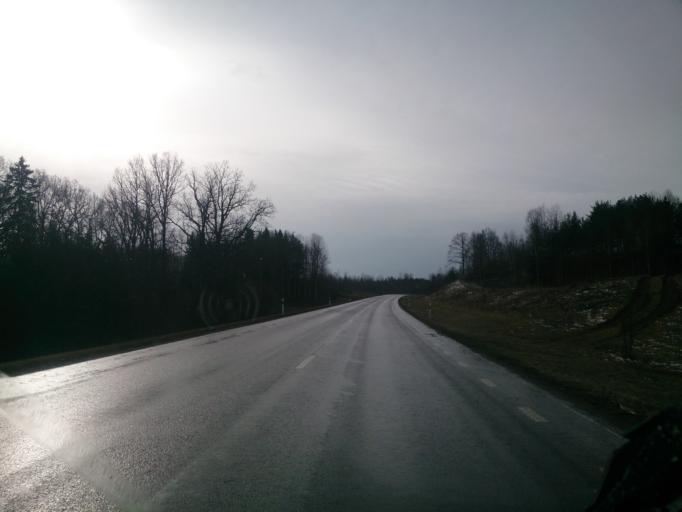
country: SE
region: OEstergoetland
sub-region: Atvidabergs Kommun
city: Atvidaberg
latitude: 58.1931
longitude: 16.0214
